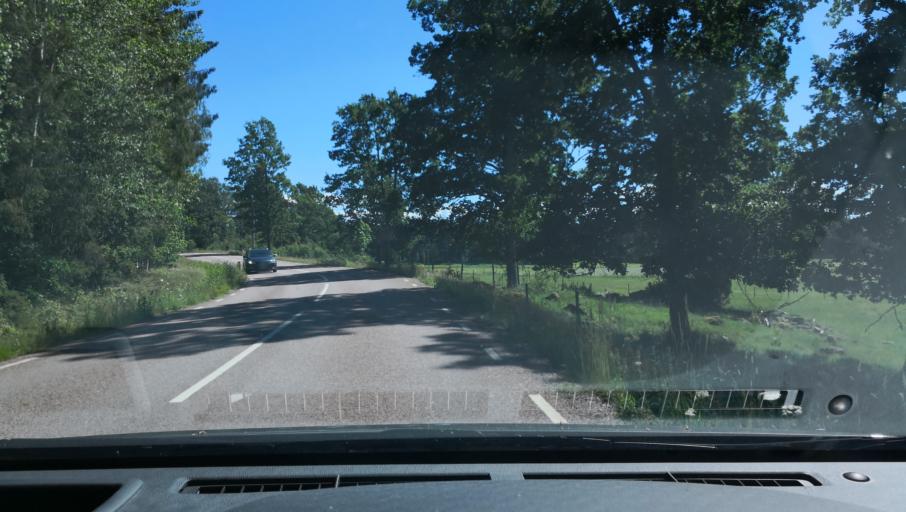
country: SE
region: Vaestmanland
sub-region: Arboga Kommun
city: Tyringe
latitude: 59.3011
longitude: 16.0192
